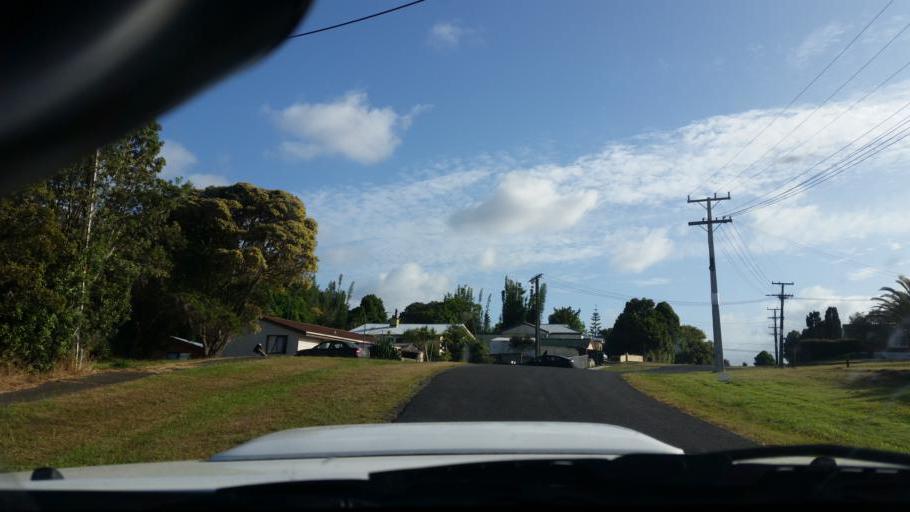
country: NZ
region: Northland
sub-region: Kaipara District
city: Dargaville
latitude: -35.9351
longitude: 173.8588
